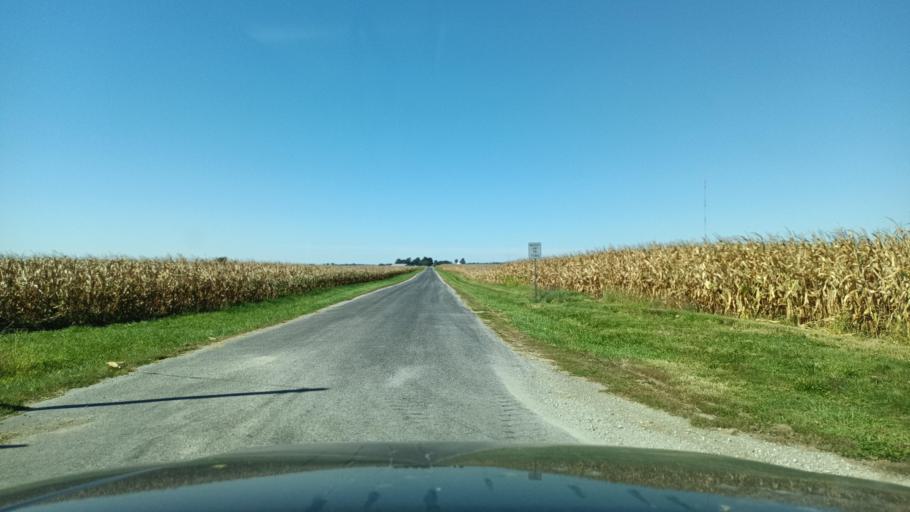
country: US
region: Illinois
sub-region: Champaign County
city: Mahomet
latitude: 40.0979
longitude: -88.4254
